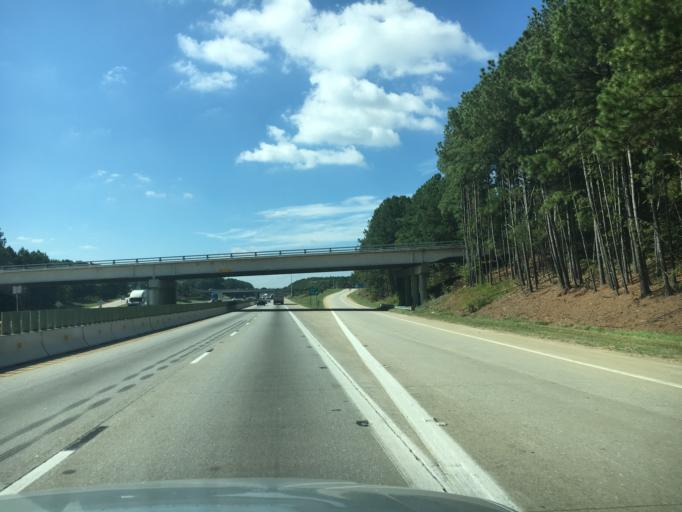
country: US
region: South Carolina
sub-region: Spartanburg County
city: Southern Shops
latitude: 35.0010
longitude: -81.9890
